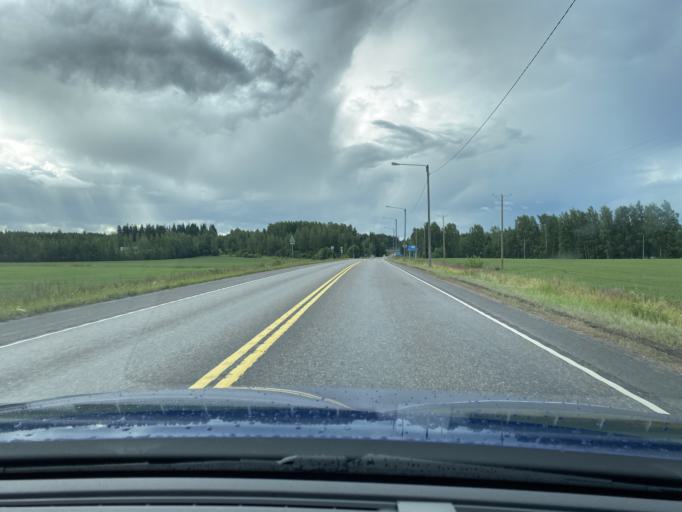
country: FI
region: Uusimaa
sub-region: Helsinki
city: Hyvinge
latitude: 60.5677
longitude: 24.8090
